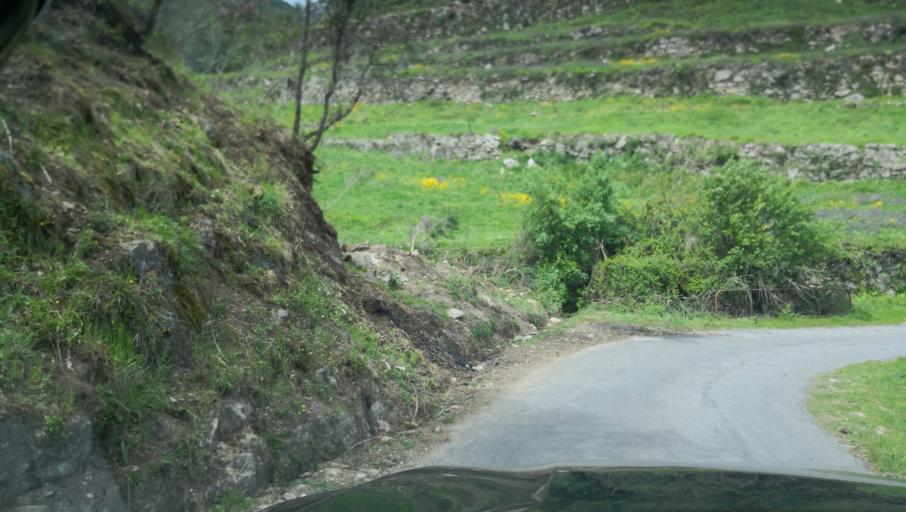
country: PT
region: Vila Real
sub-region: Vila Real
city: Vila Real
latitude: 41.3116
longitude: -7.8004
